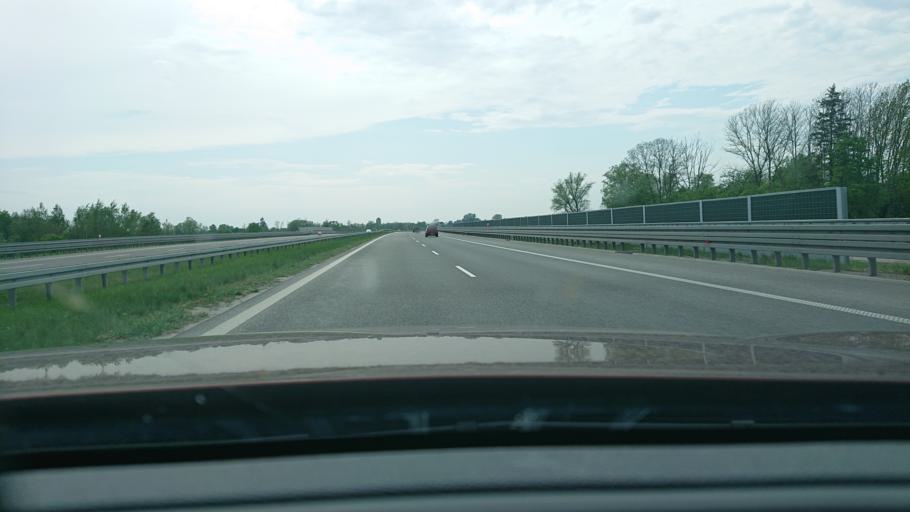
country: PL
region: Subcarpathian Voivodeship
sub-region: Powiat lancucki
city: Czarna
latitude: 50.0957
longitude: 22.2066
